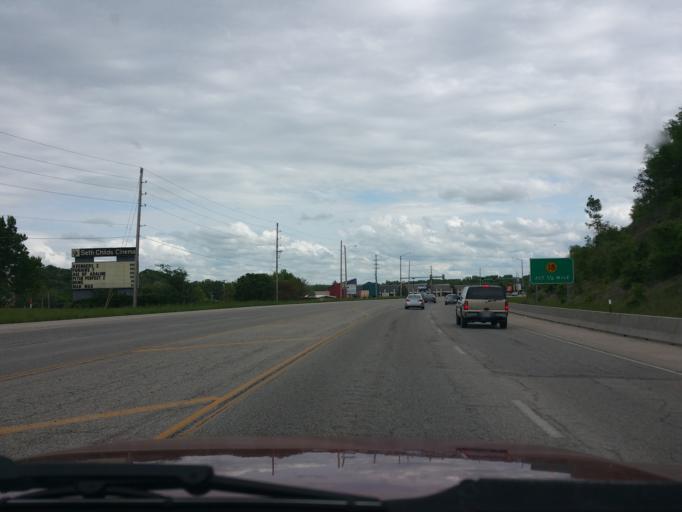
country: US
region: Kansas
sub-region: Riley County
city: Manhattan
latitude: 39.1781
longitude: -96.6061
